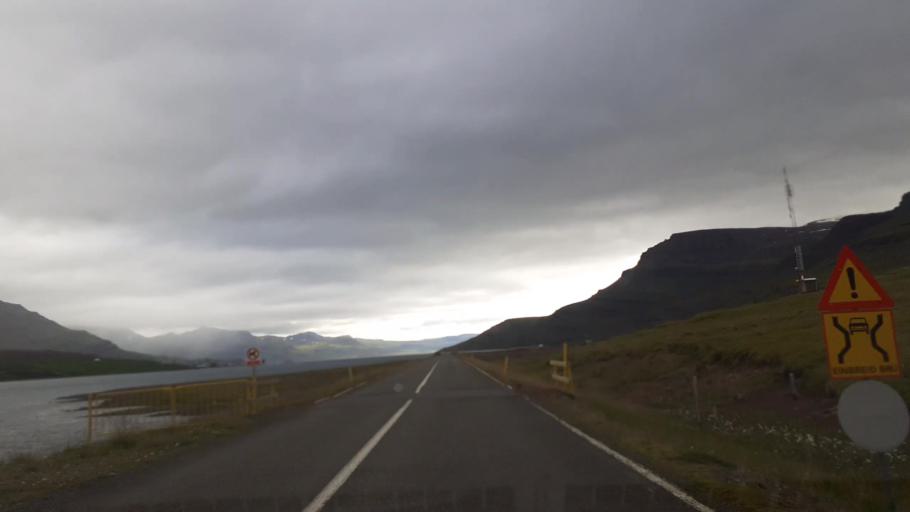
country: IS
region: East
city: Reydarfjoerdur
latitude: 65.0171
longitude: -14.2111
